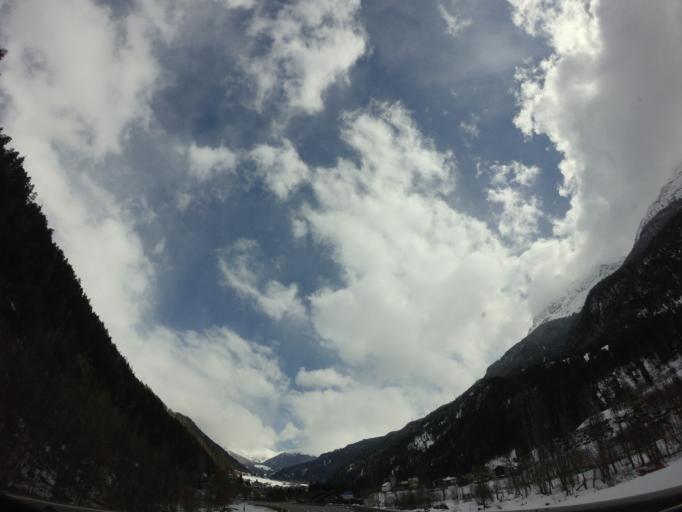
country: AT
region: Tyrol
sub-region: Politischer Bezirk Landeck
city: Nauders
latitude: 46.8571
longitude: 10.4222
